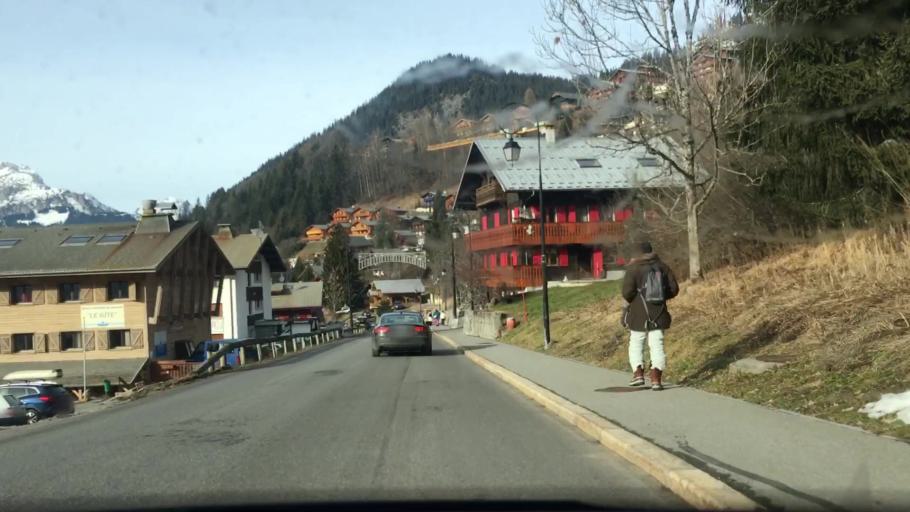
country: FR
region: Rhone-Alpes
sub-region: Departement de la Haute-Savoie
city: Chatel
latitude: 46.2737
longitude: 6.8373
